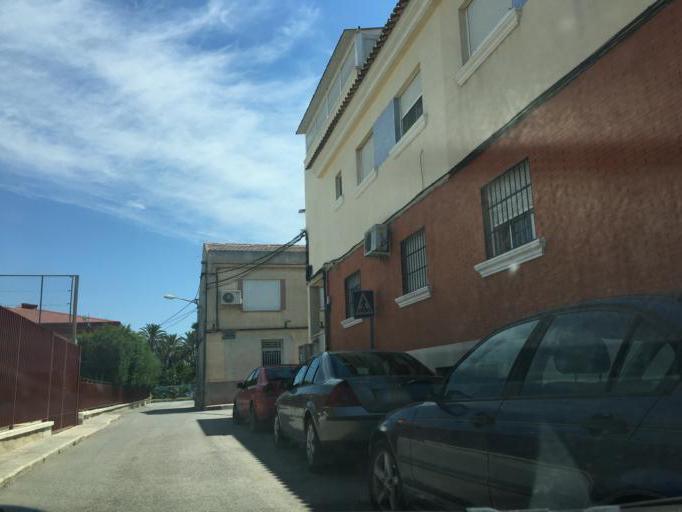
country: ES
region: Murcia
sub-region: Murcia
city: Santomera
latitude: 38.0164
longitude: -1.0541
